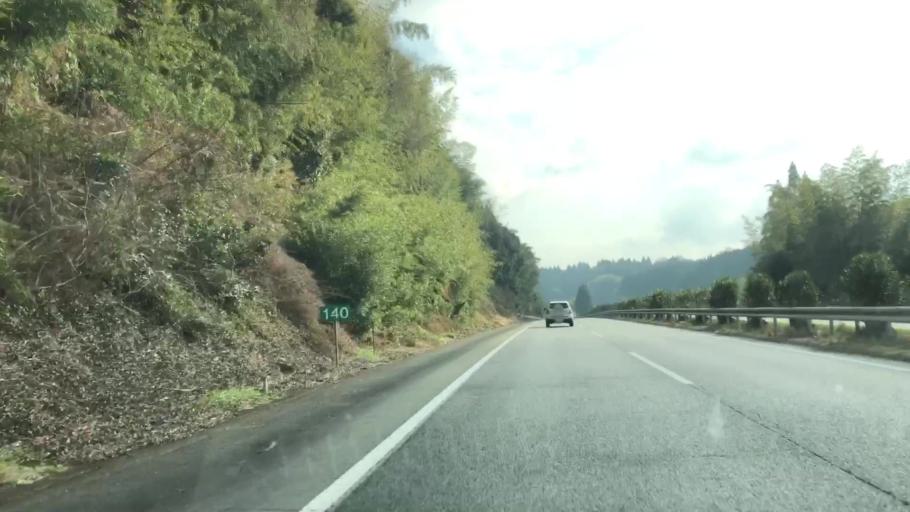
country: JP
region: Kumamoto
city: Yamaga
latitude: 33.0363
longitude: 130.5716
